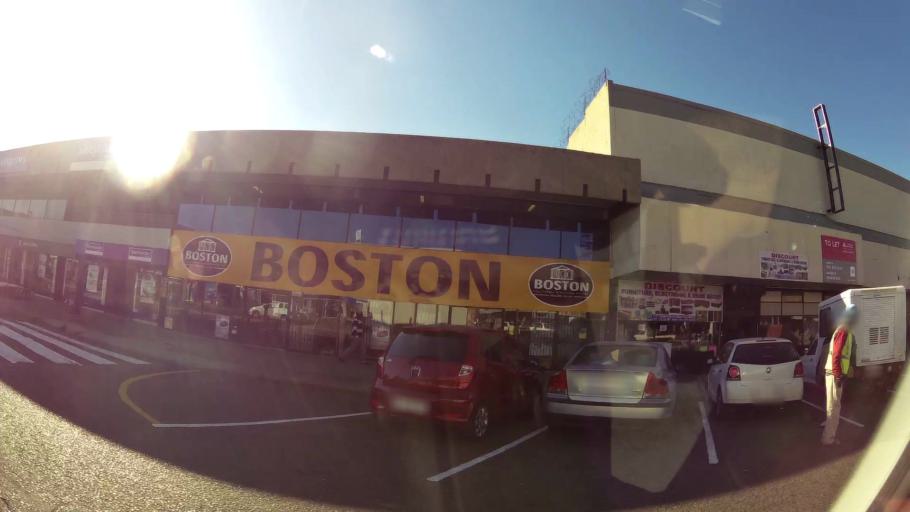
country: ZA
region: Gauteng
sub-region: Ekurhuleni Metropolitan Municipality
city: Germiston
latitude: -26.2684
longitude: 28.1221
